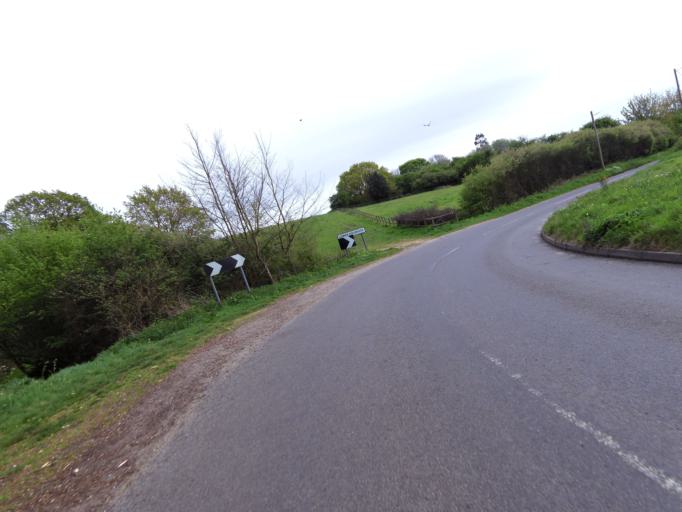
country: GB
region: England
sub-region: Suffolk
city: Ipswich
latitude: 51.9734
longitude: 1.1687
